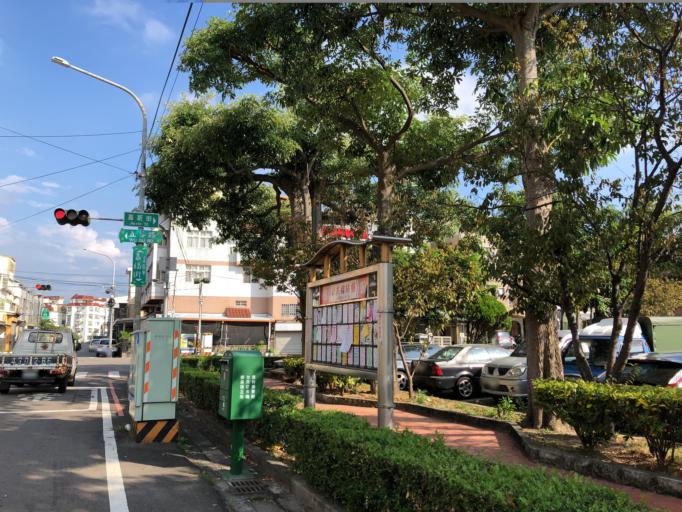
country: TW
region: Taiwan
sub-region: Miaoli
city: Miaoli
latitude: 24.5771
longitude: 120.8300
